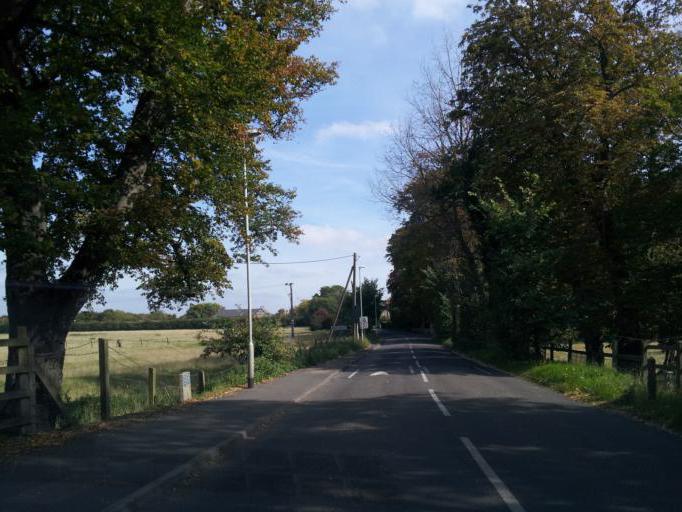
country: GB
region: England
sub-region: Cambridgeshire
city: Histon
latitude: 52.2661
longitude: 0.0781
